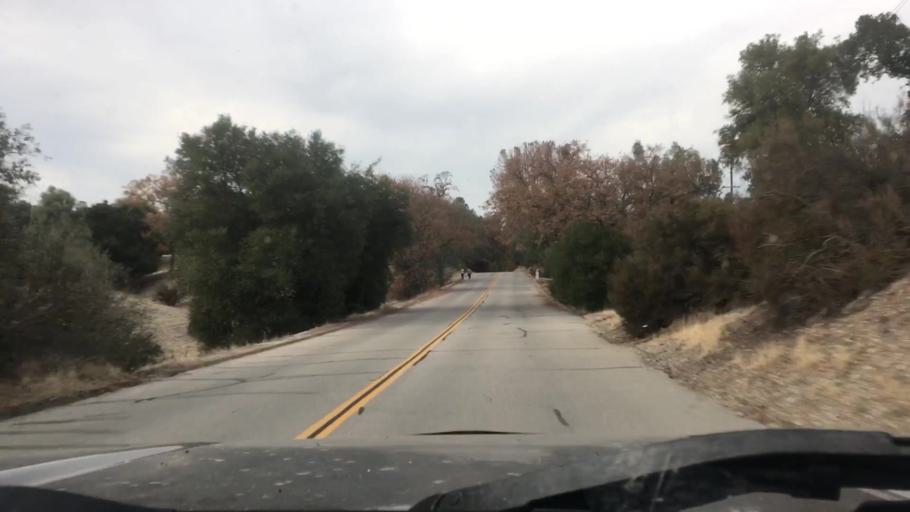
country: US
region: California
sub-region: San Luis Obispo County
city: Atascadero
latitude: 35.4458
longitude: -120.6471
